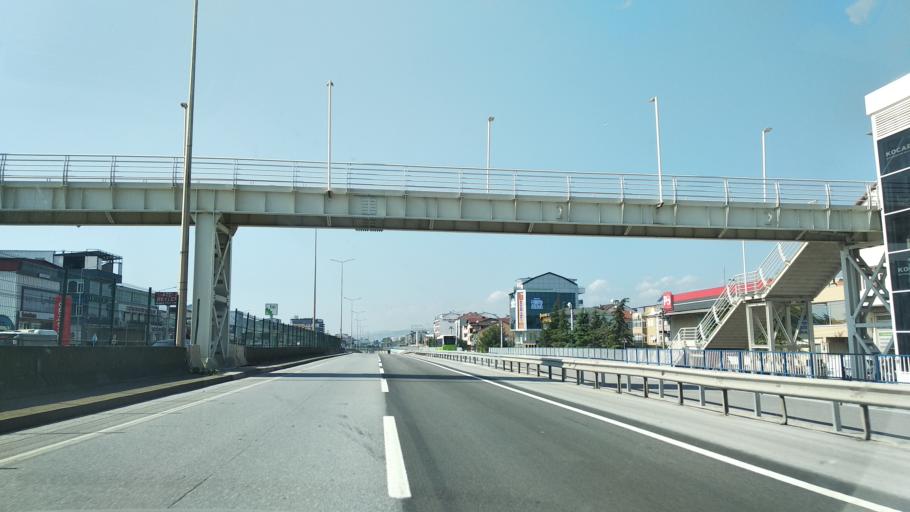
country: TR
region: Kocaeli
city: Kosekoy
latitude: 40.7527
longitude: 30.0288
